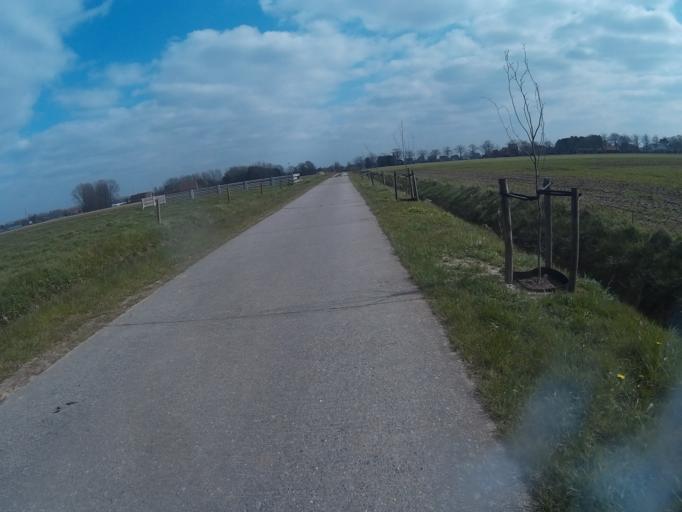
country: BE
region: Flanders
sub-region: Provincie Oost-Vlaanderen
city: Eeklo
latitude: 51.1559
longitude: 3.5271
